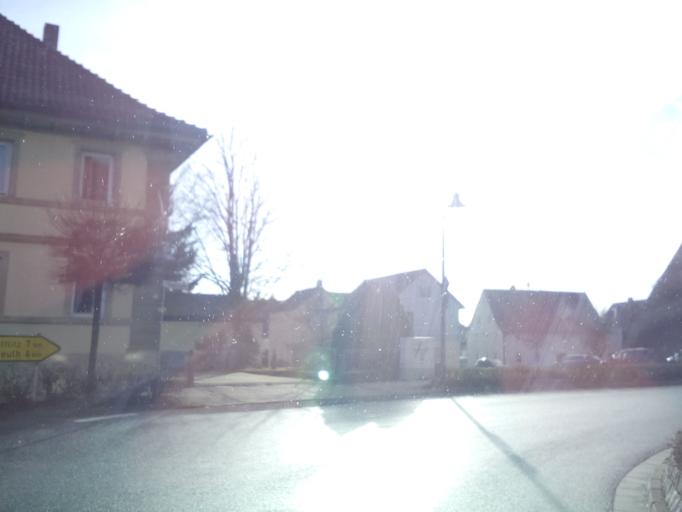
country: DE
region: Bavaria
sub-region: Upper Franconia
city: Weidhausen bei Coburg
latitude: 50.2041
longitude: 11.1405
